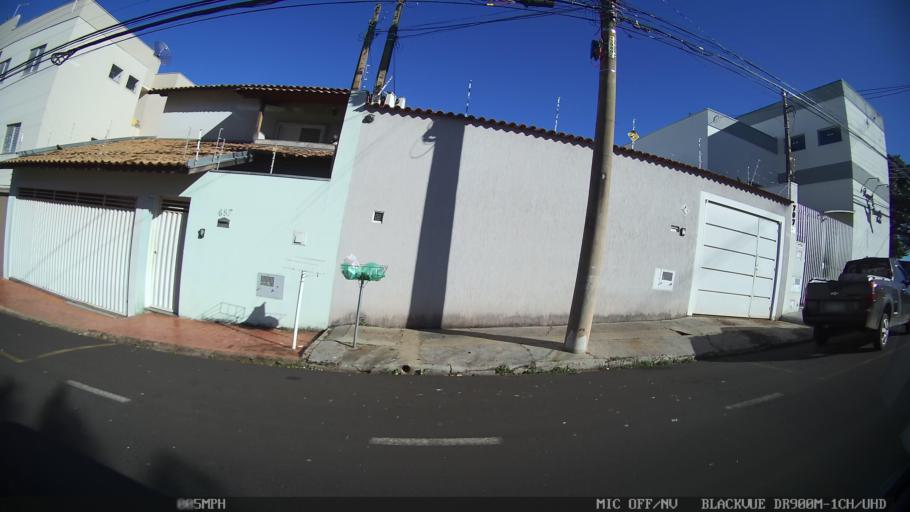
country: BR
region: Sao Paulo
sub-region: Franca
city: Franca
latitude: -20.5465
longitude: -47.4069
